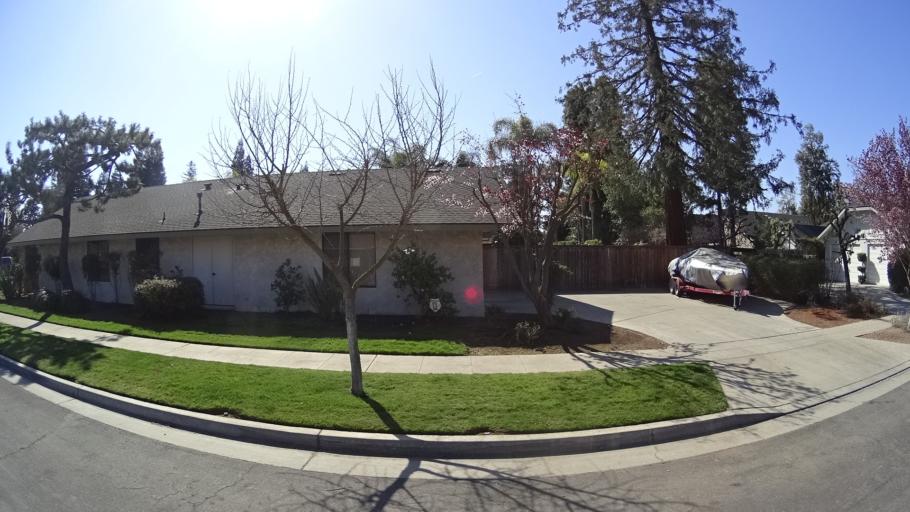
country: US
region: California
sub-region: Fresno County
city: Fresno
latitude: 36.8423
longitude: -119.8211
